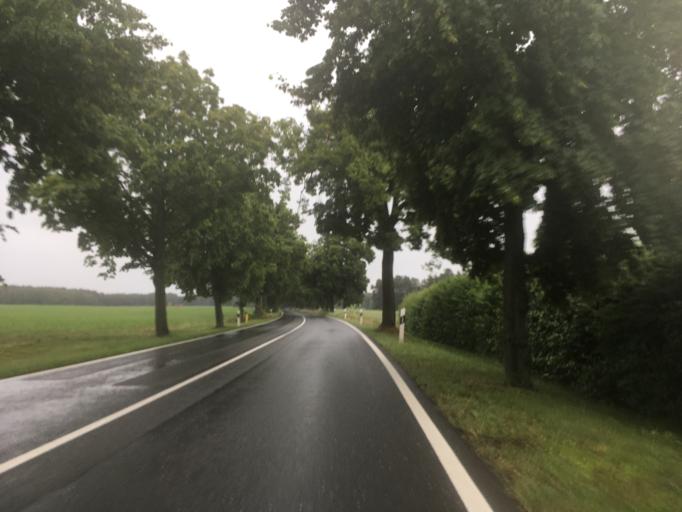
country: DE
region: Brandenburg
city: Marienwerder
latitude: 52.8948
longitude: 13.5382
